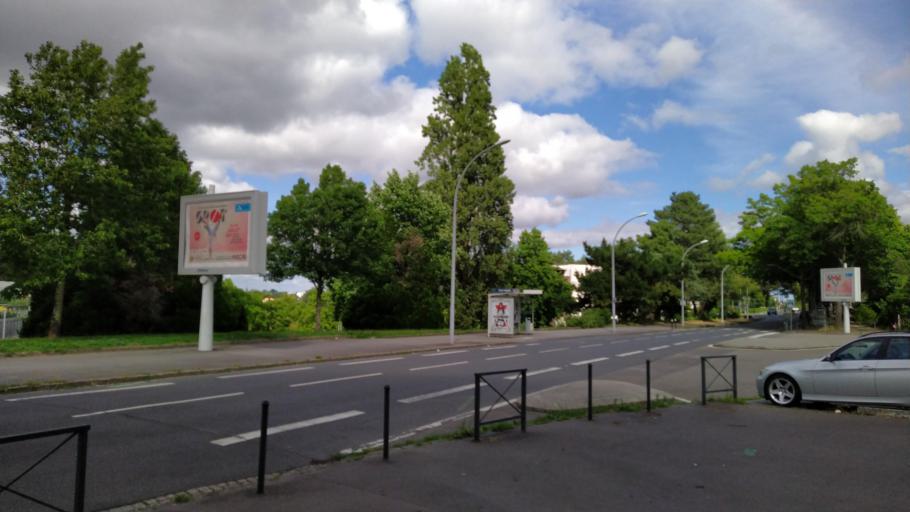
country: FR
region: Pays de la Loire
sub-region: Departement de la Loire-Atlantique
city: Nantes
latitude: 47.2225
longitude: -1.5974
